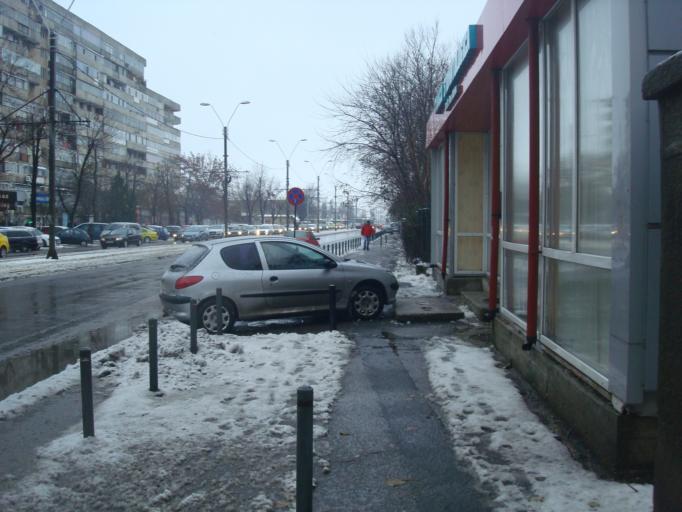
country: RO
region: Bucuresti
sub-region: Municipiul Bucuresti
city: Bucuresti
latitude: 44.3818
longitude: 26.0923
